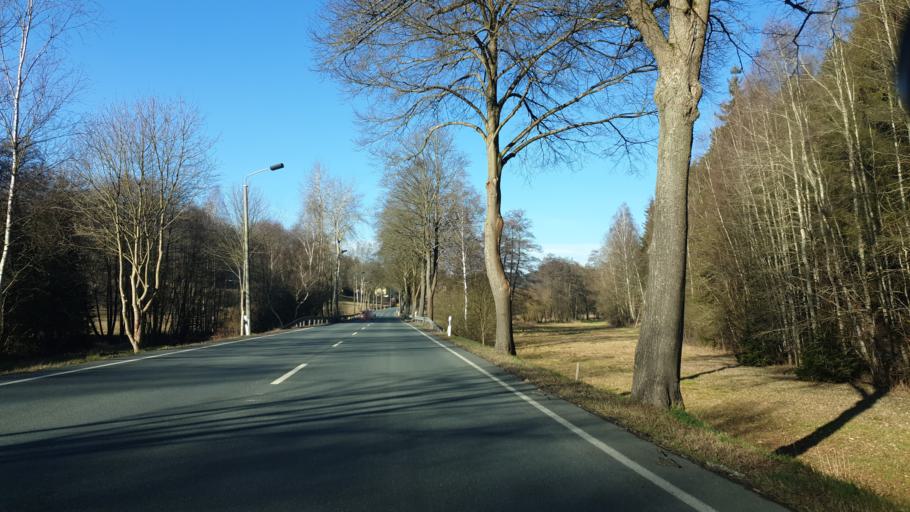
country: DE
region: Saxony
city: Adorf
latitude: 50.2845
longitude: 12.2760
